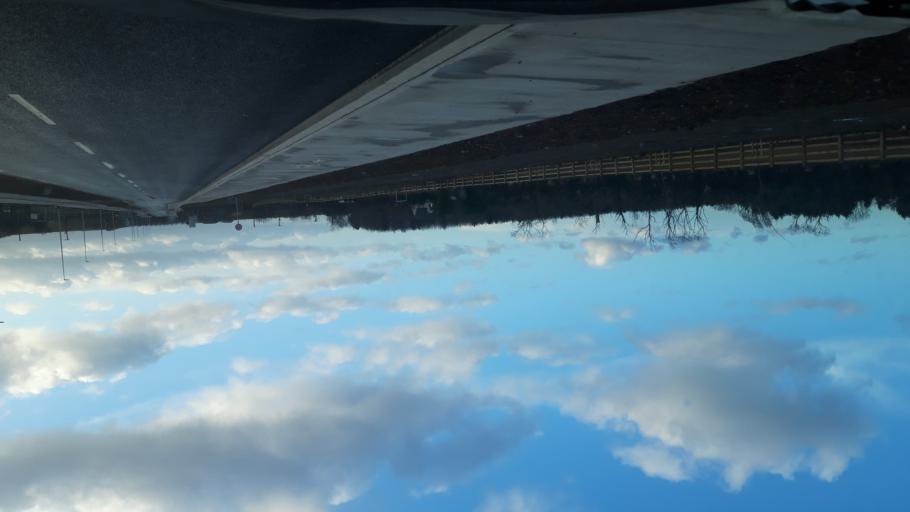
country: IE
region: Leinster
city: Donabate
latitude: 53.4853
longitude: -6.1372
